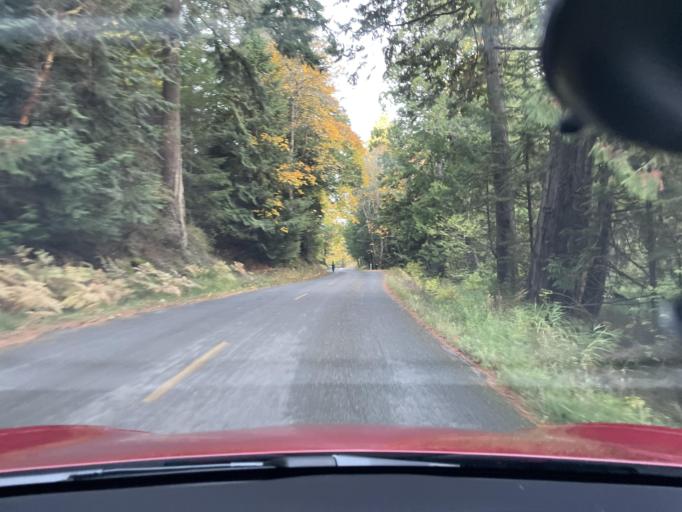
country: US
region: Washington
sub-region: San Juan County
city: Friday Harbor
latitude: 48.5273
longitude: -123.1486
